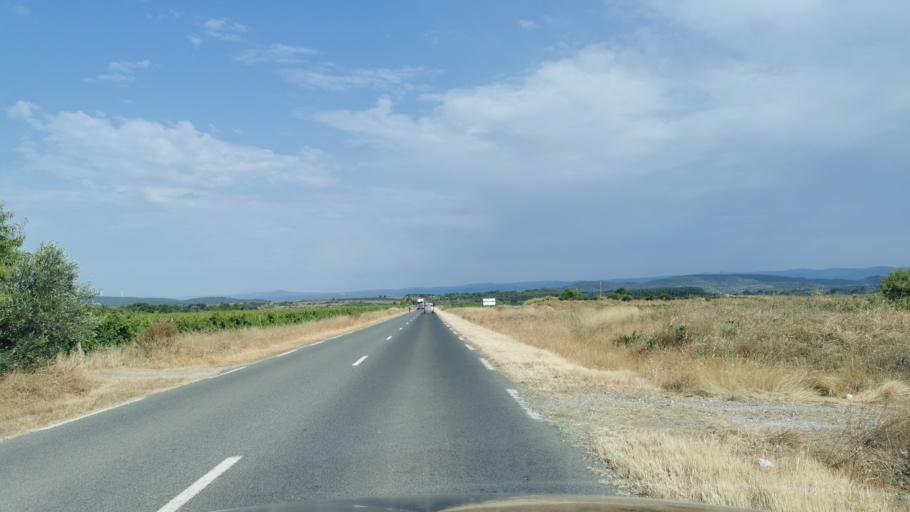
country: FR
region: Languedoc-Roussillon
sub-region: Departement de l'Aude
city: Ginestas
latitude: 43.2792
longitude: 2.8811
